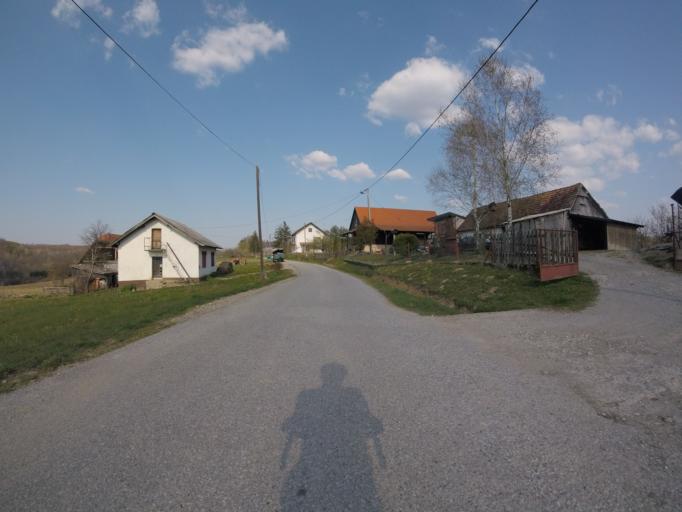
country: HR
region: Sisacko-Moslavacka
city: Glina
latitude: 45.5030
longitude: 15.9990
